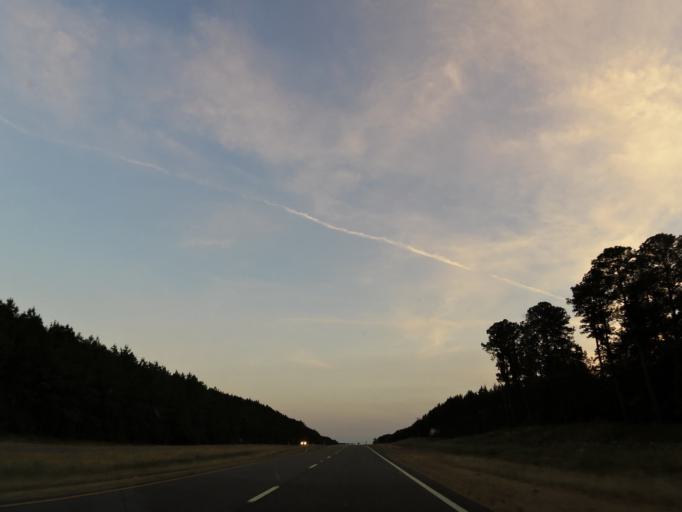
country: US
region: Mississippi
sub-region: Kemper County
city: De Kalb
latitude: 32.7509
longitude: -88.4662
